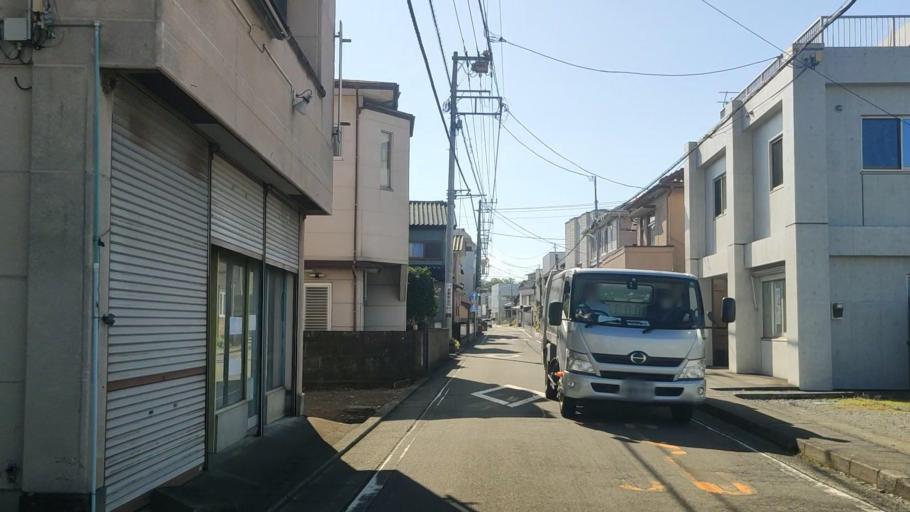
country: JP
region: Shizuoka
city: Mishima
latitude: 35.0145
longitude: 138.9460
